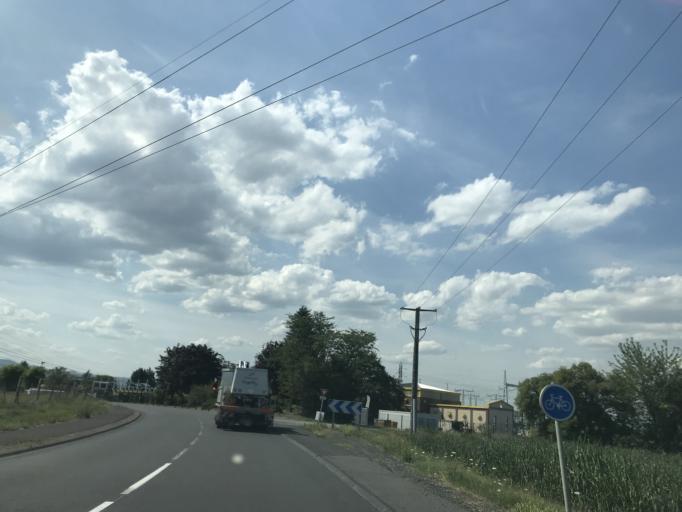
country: FR
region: Auvergne
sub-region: Departement du Puy-de-Dome
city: Malintrat
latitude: 45.8078
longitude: 3.1970
